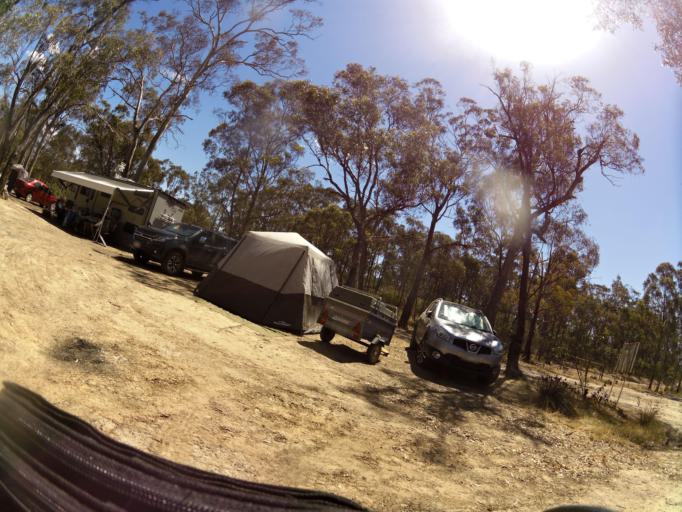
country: AU
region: Victoria
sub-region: Campaspe
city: Kyabram
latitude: -36.8555
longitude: 145.0674
